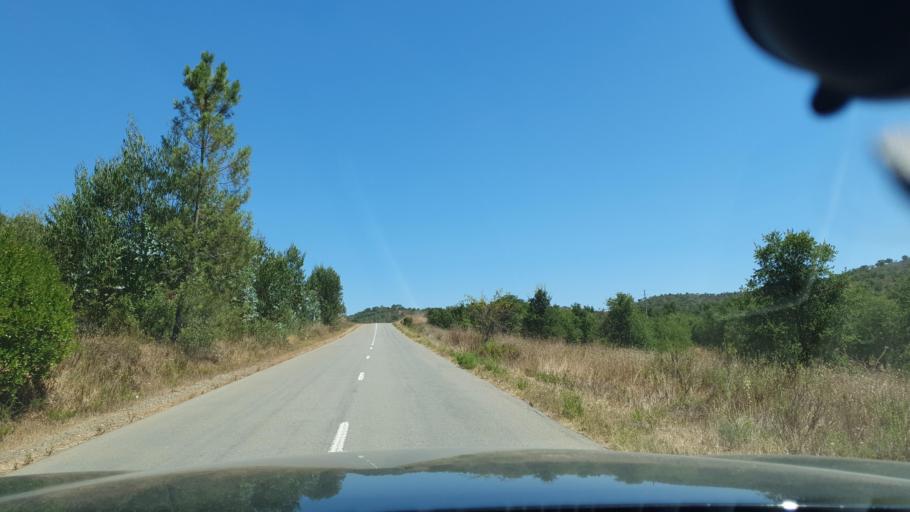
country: PT
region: Beja
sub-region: Odemira
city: Odemira
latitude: 37.5223
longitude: -8.4733
